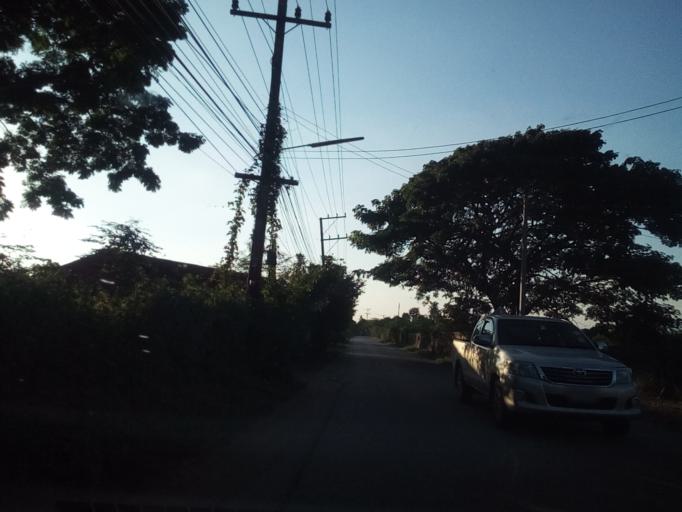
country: TH
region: Lamphun
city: Ban Thi
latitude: 18.6344
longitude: 99.0499
